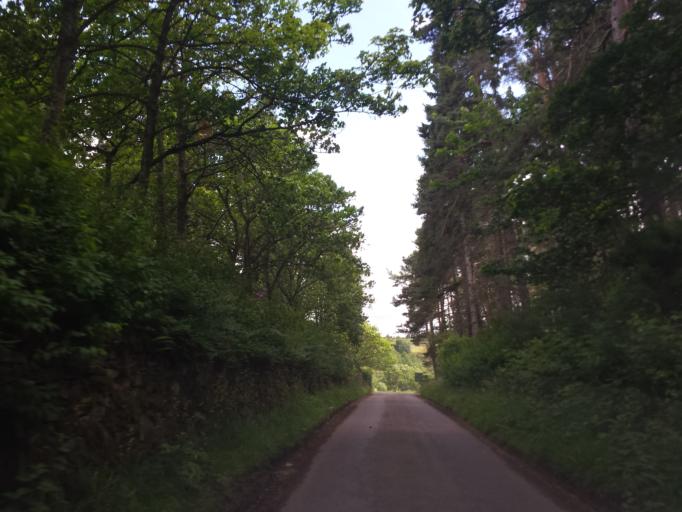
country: GB
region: Scotland
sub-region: Highland
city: Fortrose
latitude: 57.4757
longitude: -4.0690
